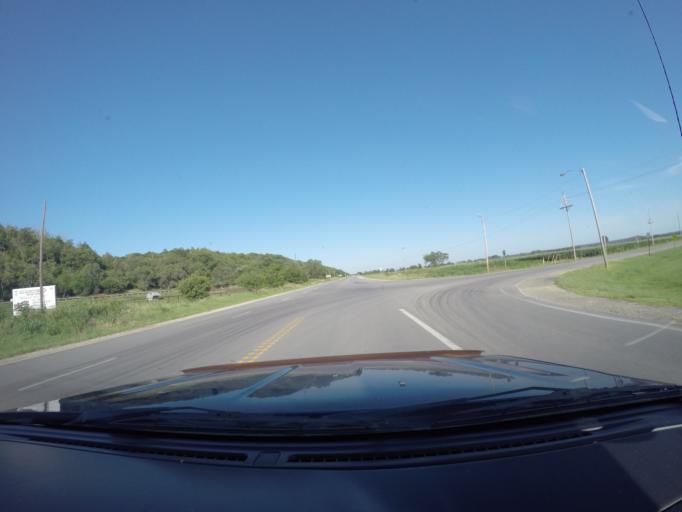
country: US
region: Kansas
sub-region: Jefferson County
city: Oskaloosa
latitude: 39.0791
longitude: -95.3821
